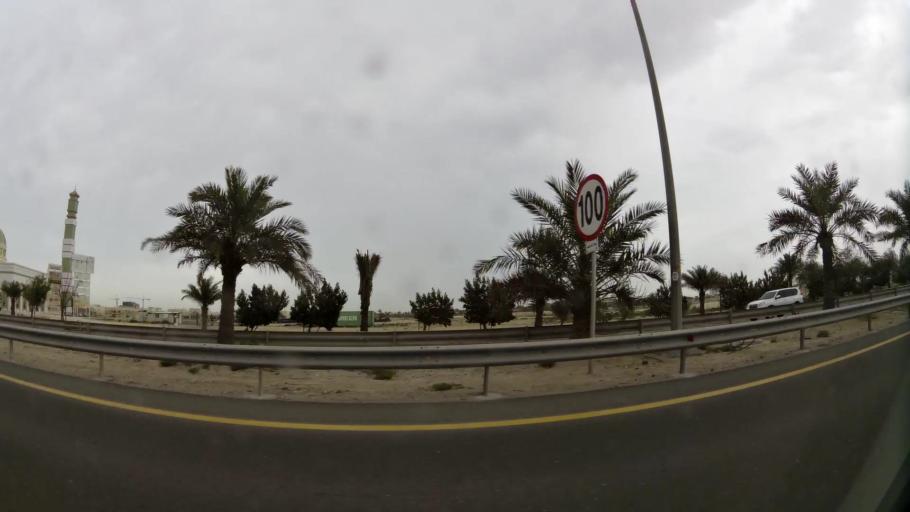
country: BH
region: Central Governorate
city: Dar Kulayb
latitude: 26.0847
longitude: 50.5395
